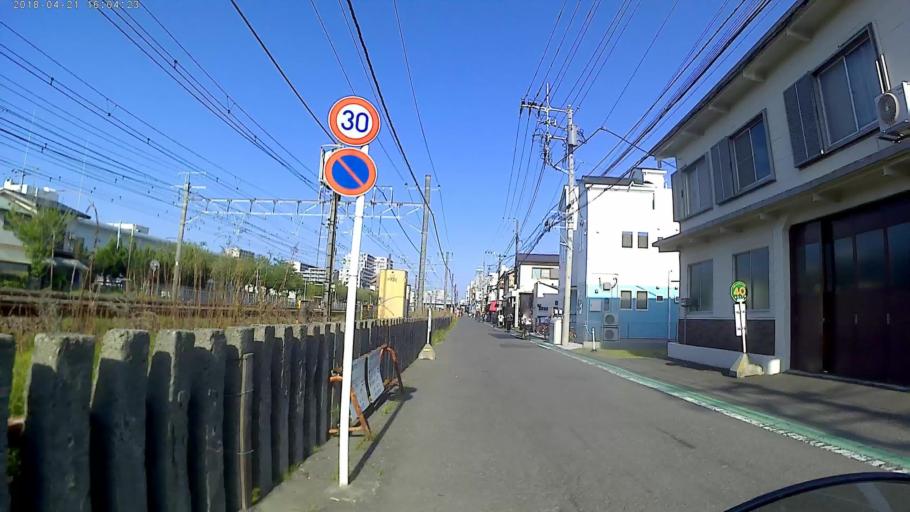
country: JP
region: Kanagawa
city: Fujisawa
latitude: 35.3364
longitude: 139.4393
